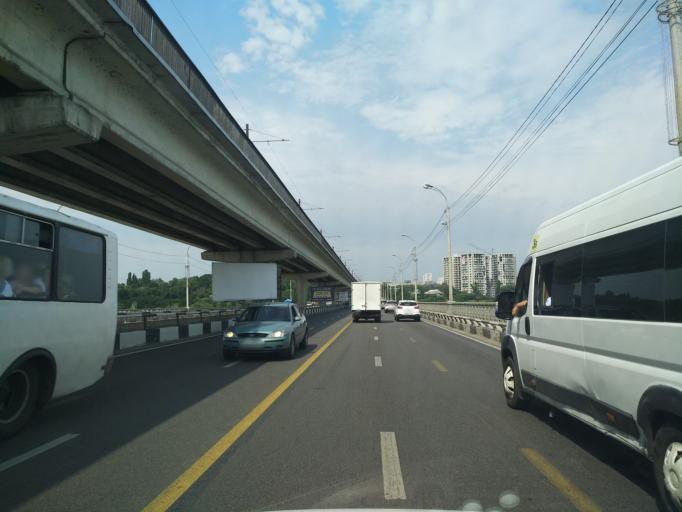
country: RU
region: Voronezj
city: Voronezh
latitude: 51.6918
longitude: 39.2406
